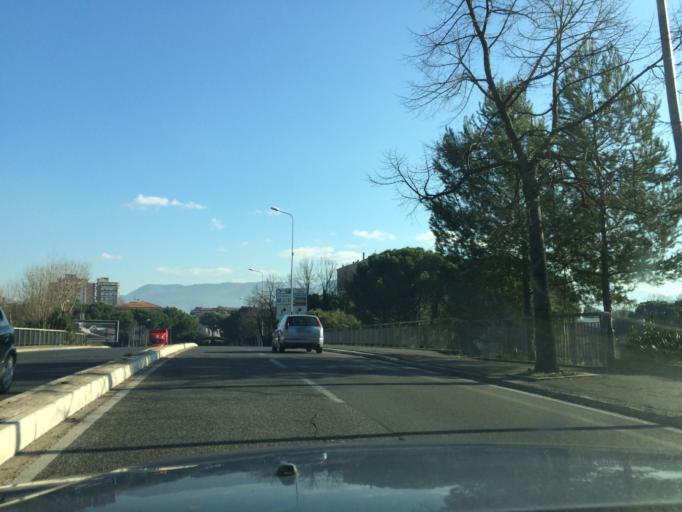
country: IT
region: Umbria
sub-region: Provincia di Terni
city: Terni
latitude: 42.5658
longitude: 12.6361
